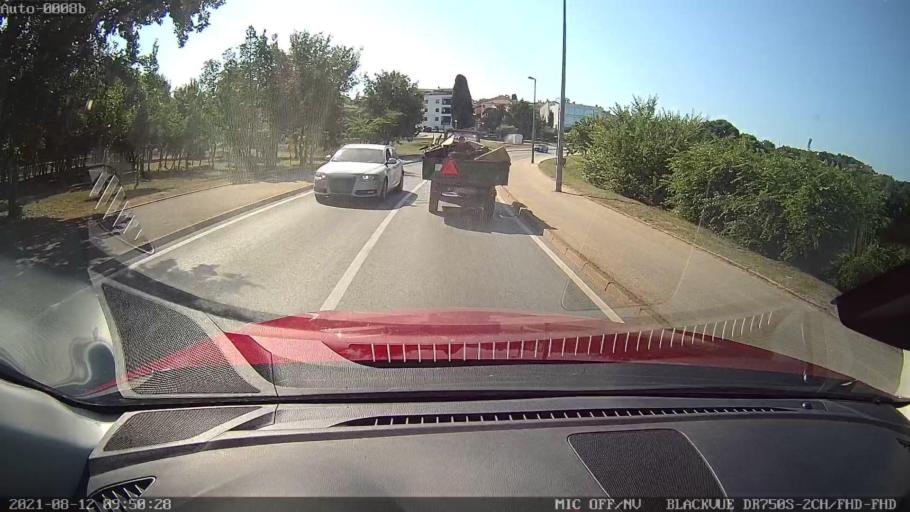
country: HR
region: Istarska
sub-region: Grad Rovinj
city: Rovinj
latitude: 45.0918
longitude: 13.6452
